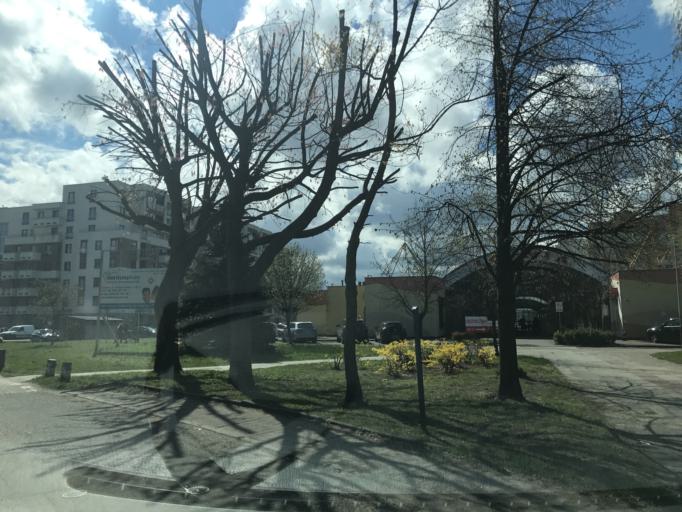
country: PL
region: Pomeranian Voivodeship
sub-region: Gdansk
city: Gdansk
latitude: 54.3940
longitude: 18.6105
